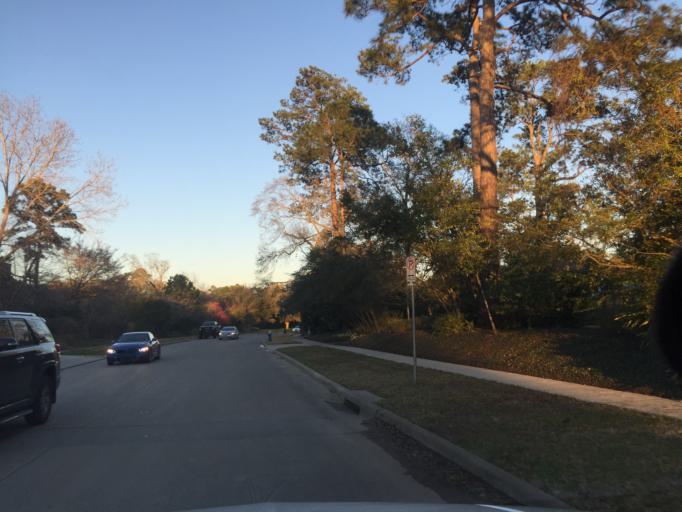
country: US
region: Texas
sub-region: Harris County
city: West University Place
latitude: 29.7513
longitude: -95.4245
